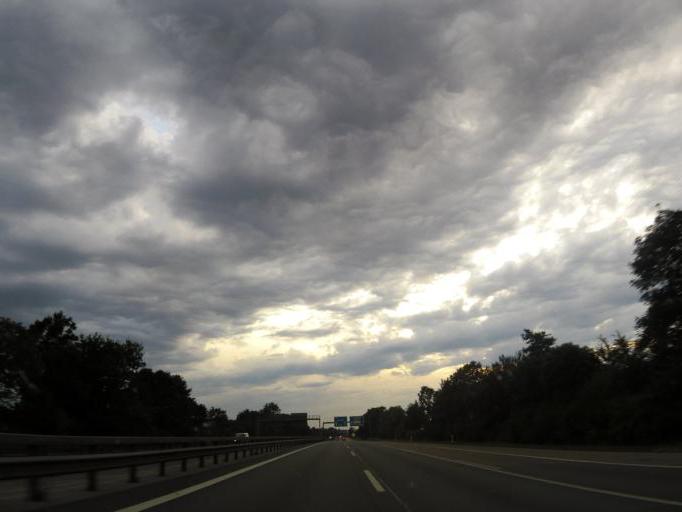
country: DE
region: Bavaria
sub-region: Upper Bavaria
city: Raubling
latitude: 47.8082
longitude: 12.1137
